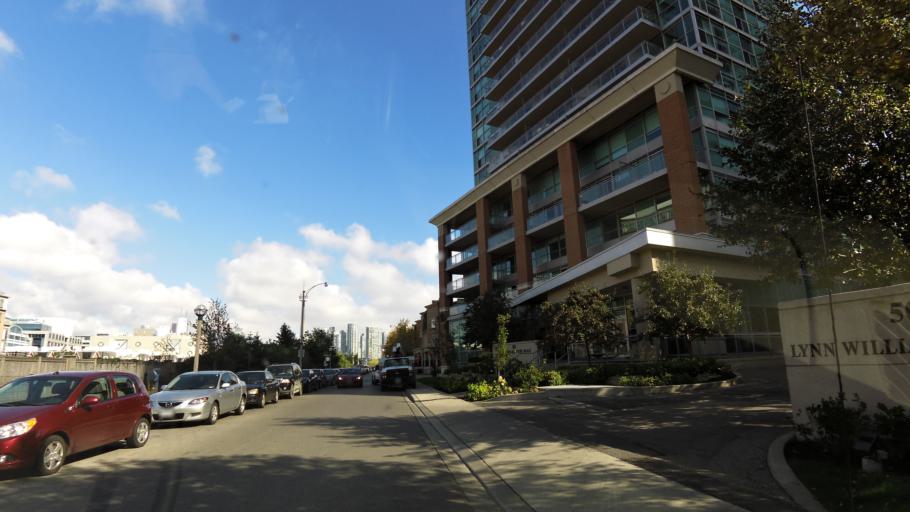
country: CA
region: Ontario
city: Toronto
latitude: 43.6402
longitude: -79.4153
